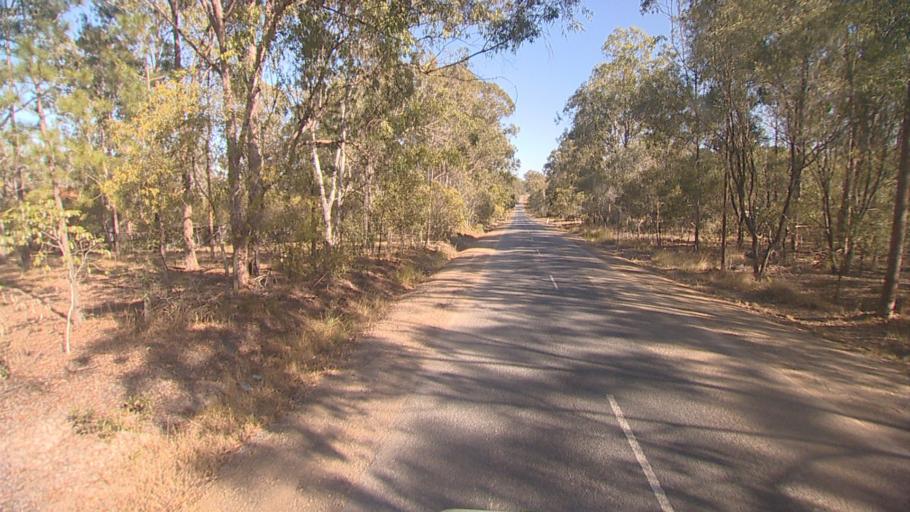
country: AU
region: Queensland
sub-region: Logan
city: Cedar Vale
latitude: -27.8425
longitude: 153.0473
